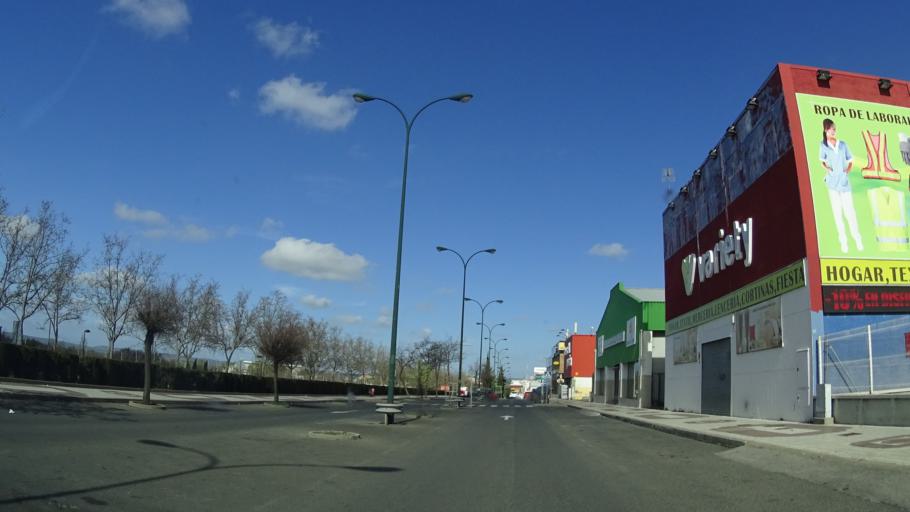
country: ES
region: Castille-La Mancha
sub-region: Provincia de Ciudad Real
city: Puertollano
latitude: 38.6989
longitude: -4.1049
